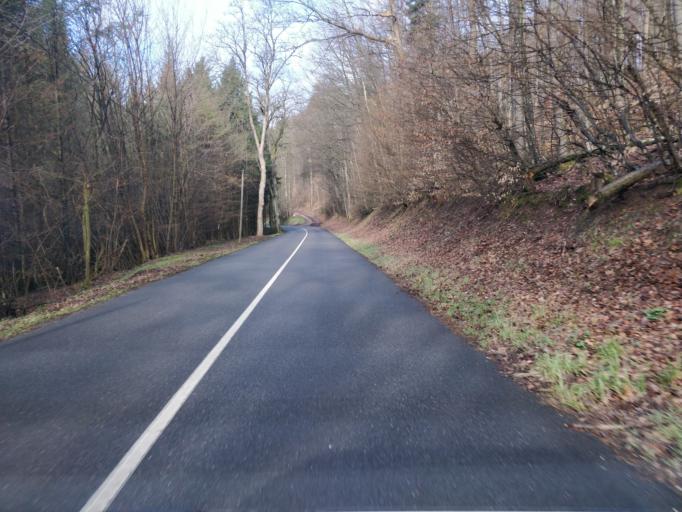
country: FR
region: Lorraine
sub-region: Departement de la Moselle
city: Soucht
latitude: 48.9189
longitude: 7.3145
